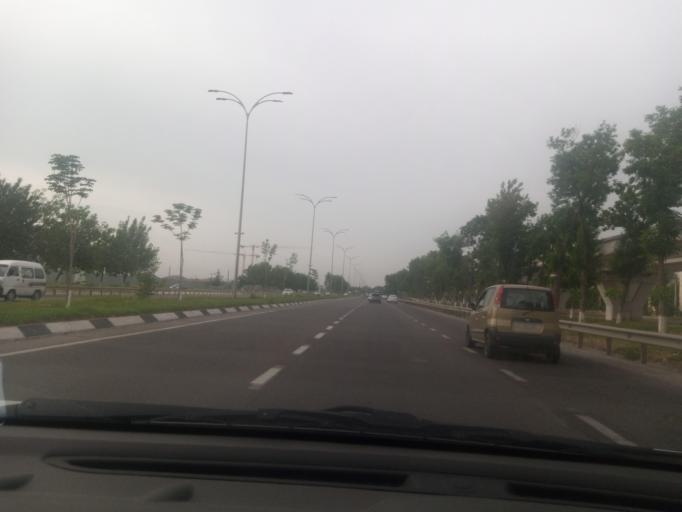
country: UZ
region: Toshkent Shahri
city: Bektemir
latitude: 41.2795
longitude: 69.3611
